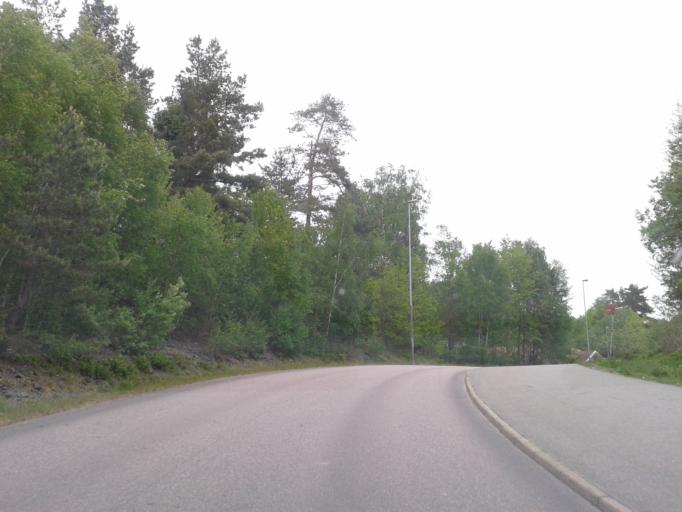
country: SE
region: Vaestra Goetaland
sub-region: Kungalvs Kommun
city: Kungalv
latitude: 57.8881
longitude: 11.9531
